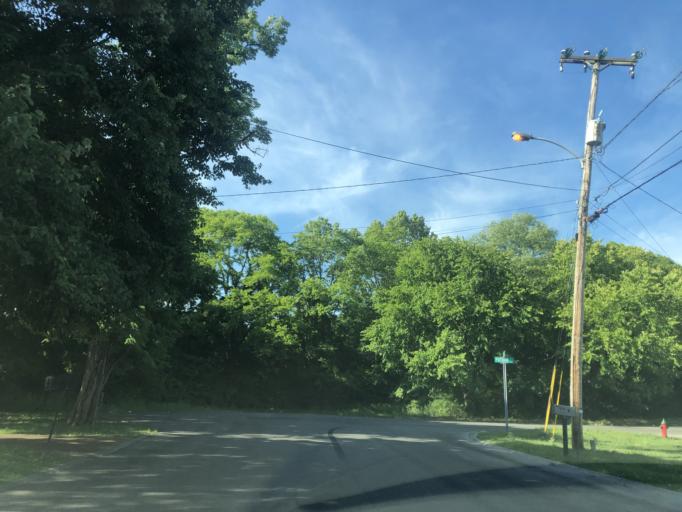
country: US
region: Tennessee
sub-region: Davidson County
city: Nashville
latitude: 36.2244
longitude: -86.8493
